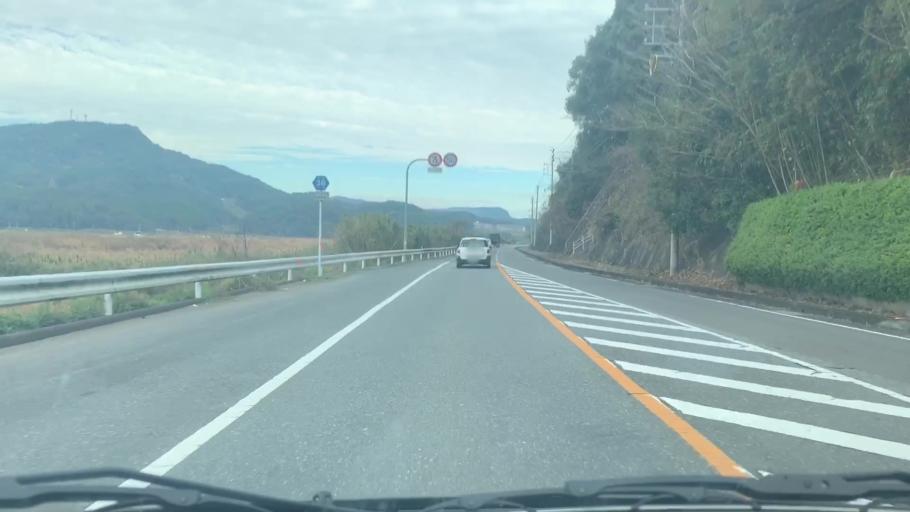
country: JP
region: Saga Prefecture
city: Imaricho-ko
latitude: 33.2718
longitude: 129.9647
